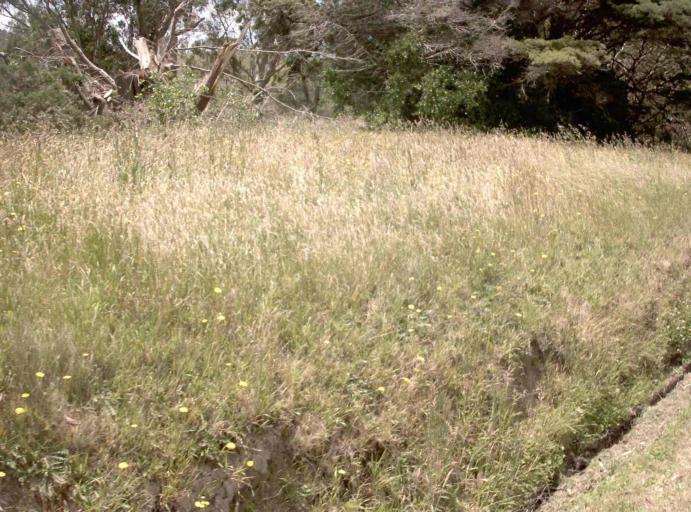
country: AU
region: Victoria
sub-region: Bass Coast
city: North Wonthaggi
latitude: -38.7173
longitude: 146.1039
